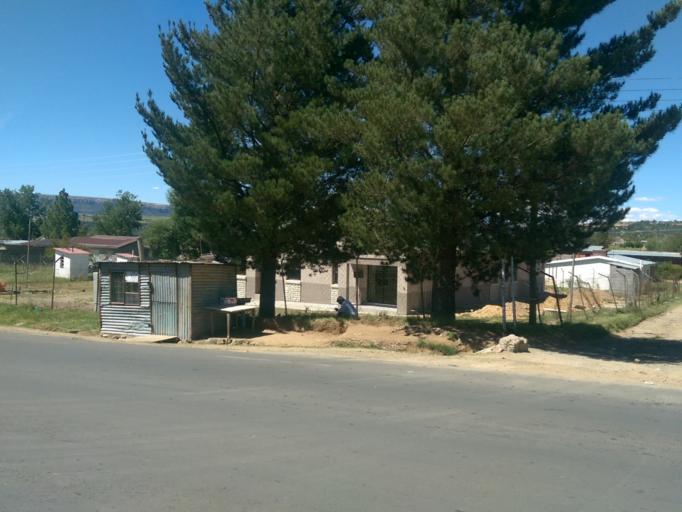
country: LS
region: Maseru
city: Maseru
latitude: -29.4156
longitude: 27.5593
